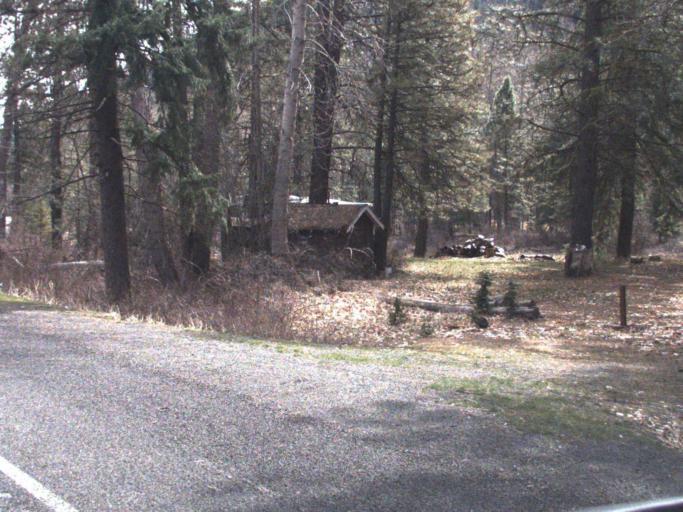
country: US
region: Washington
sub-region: Kittitas County
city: Cle Elum
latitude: 46.9014
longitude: -121.0136
